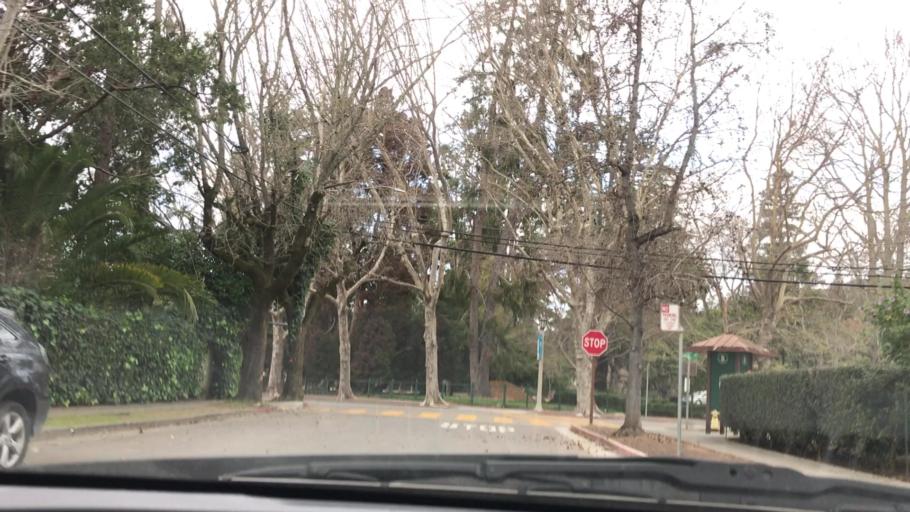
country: US
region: California
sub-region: Marin County
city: San Rafael
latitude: 37.9791
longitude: -122.5148
